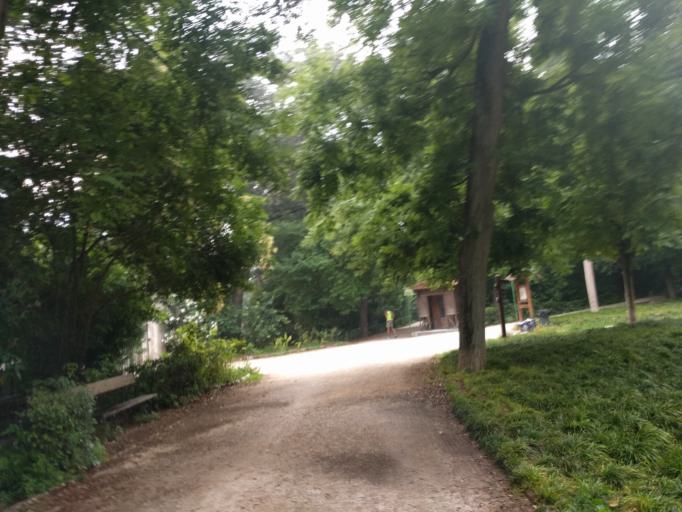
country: GR
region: Attica
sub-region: Nomarchia Athinas
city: Vyronas
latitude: 37.9728
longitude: 23.7399
